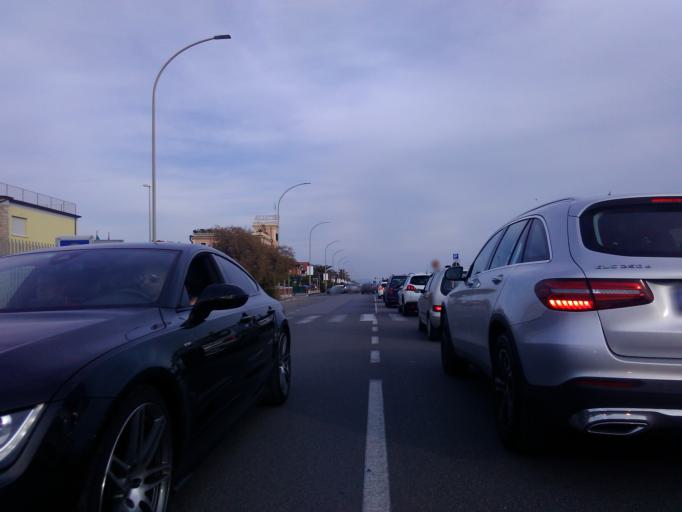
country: IT
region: Tuscany
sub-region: Provincia di Massa-Carrara
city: Massa
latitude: 44.0099
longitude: 10.0958
